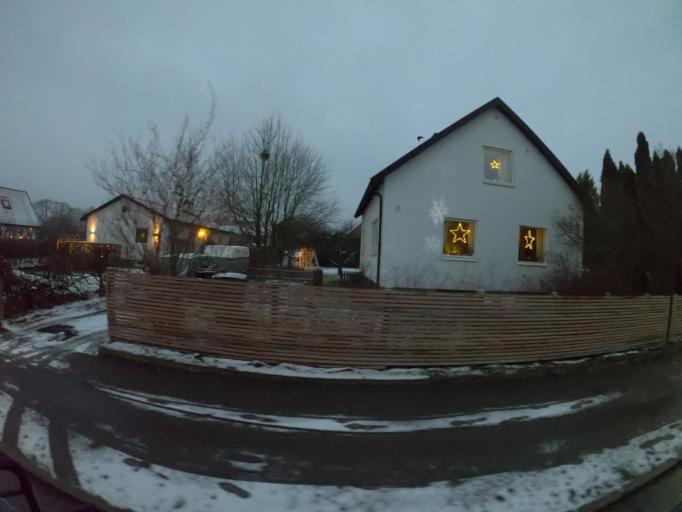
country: SE
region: Skane
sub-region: Svedala Kommun
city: Svedala
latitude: 55.5134
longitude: 13.2430
